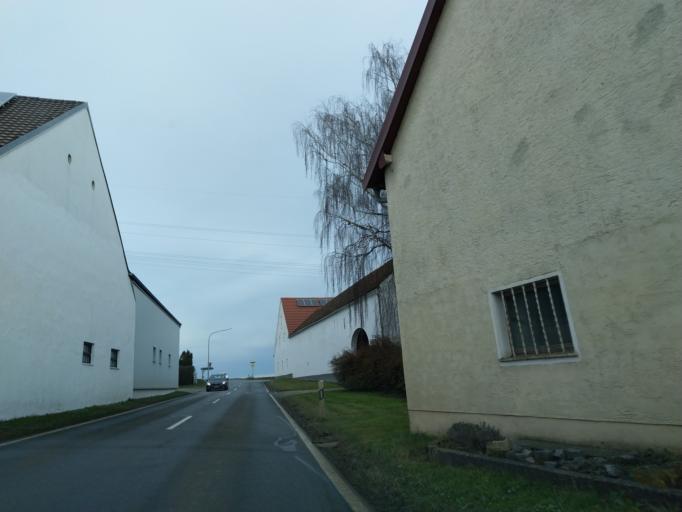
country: DE
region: Bavaria
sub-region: Lower Bavaria
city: Osterhofen
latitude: 48.6755
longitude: 12.9948
